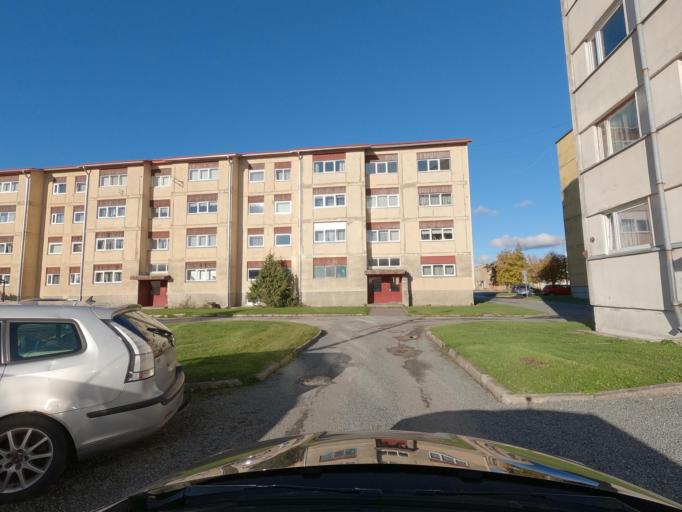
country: EE
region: Saare
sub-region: Kuressaare linn
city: Kuressaare
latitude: 58.2634
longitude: 22.4835
